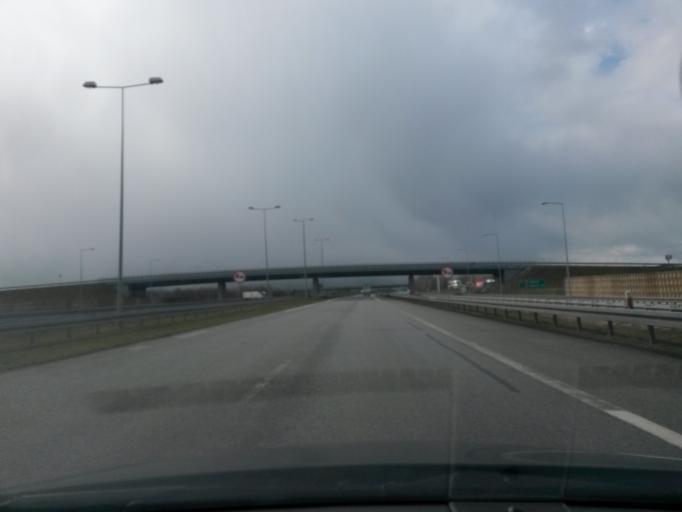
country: PL
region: Greater Poland Voivodeship
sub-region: Powiat koninski
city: Stare Miasto
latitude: 52.1623
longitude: 18.2139
